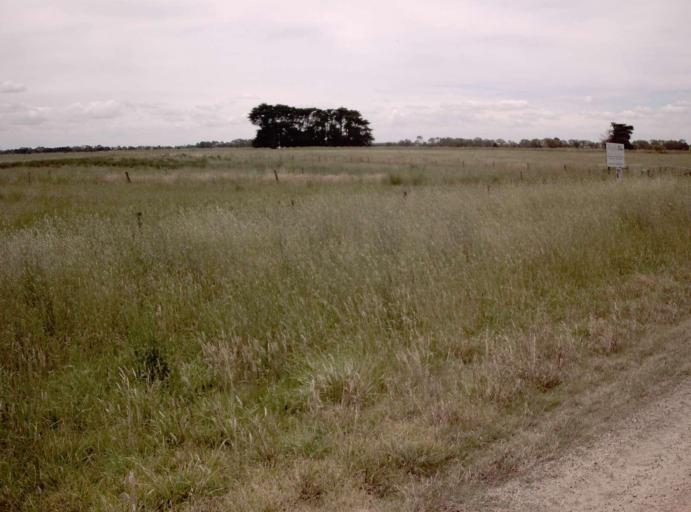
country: AU
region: Victoria
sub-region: Wellington
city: Sale
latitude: -38.0071
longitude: 147.0051
